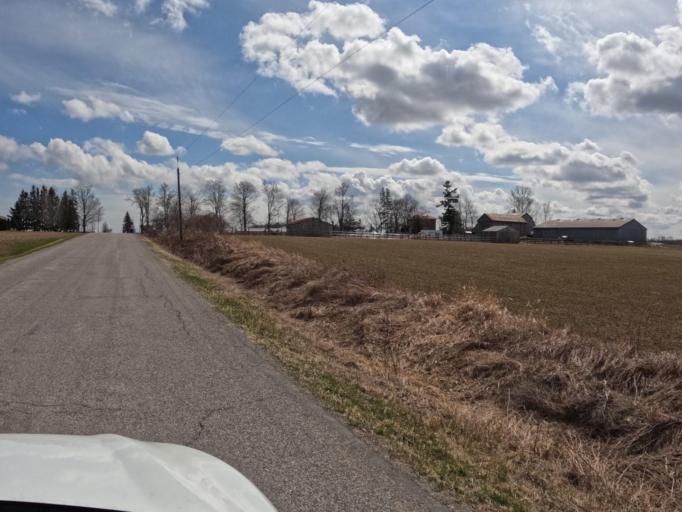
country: CA
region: Ontario
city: Norfolk County
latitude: 42.9288
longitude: -80.2008
